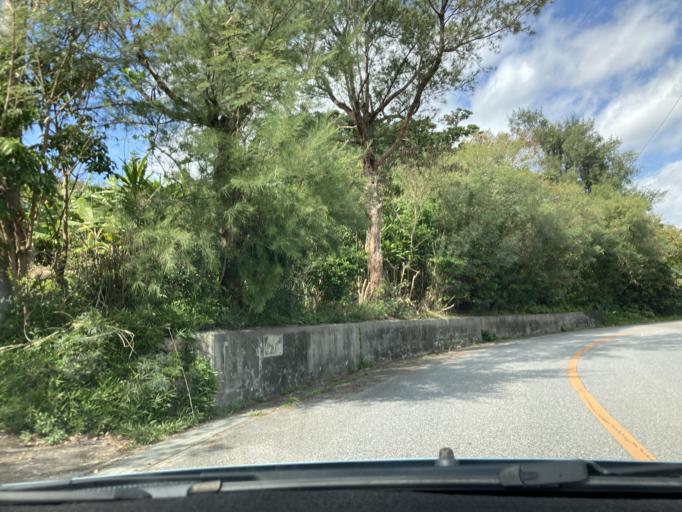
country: JP
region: Okinawa
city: Ginowan
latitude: 26.1803
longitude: 127.7663
